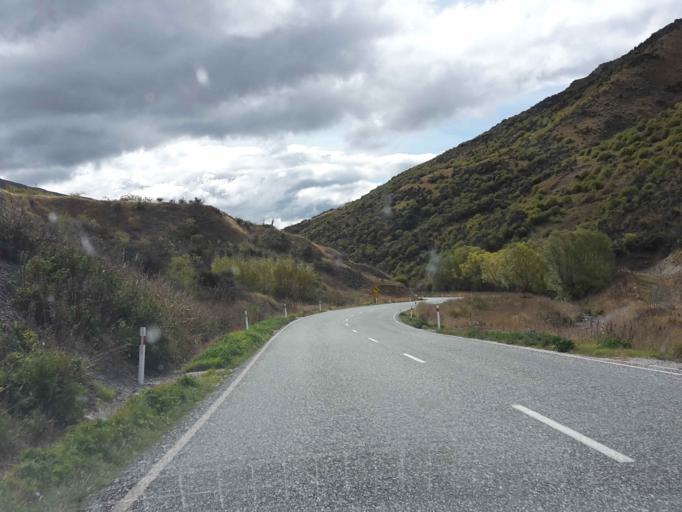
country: NZ
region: Otago
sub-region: Queenstown-Lakes District
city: Arrowtown
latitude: -44.9294
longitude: 168.9704
